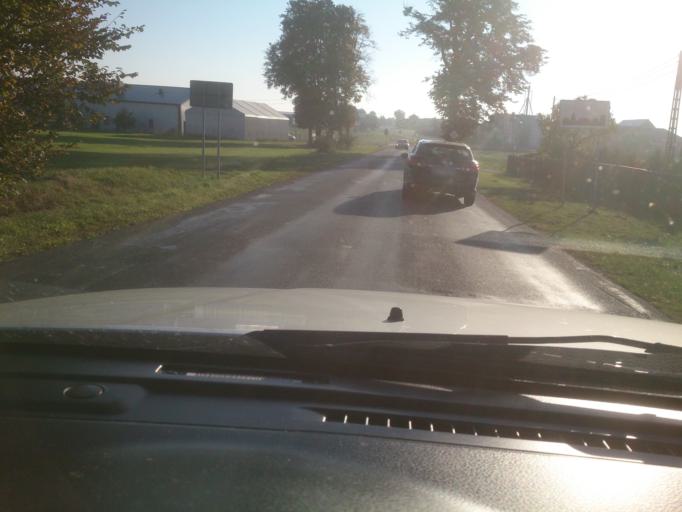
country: PL
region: Kujawsko-Pomorskie
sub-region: Powiat brodnicki
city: Brodnica
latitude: 53.2412
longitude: 19.4899
